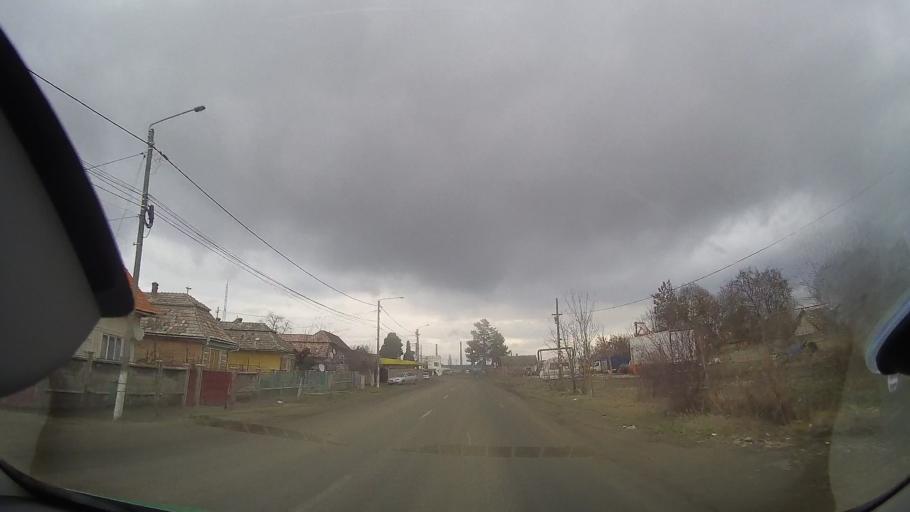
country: RO
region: Cluj
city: Turda
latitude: 46.5479
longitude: 23.7822
